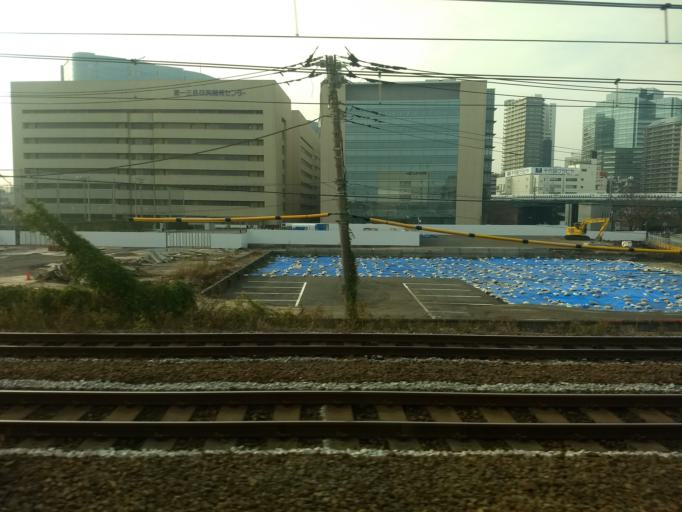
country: JP
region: Tokyo
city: Tokyo
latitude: 35.6154
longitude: 139.7363
